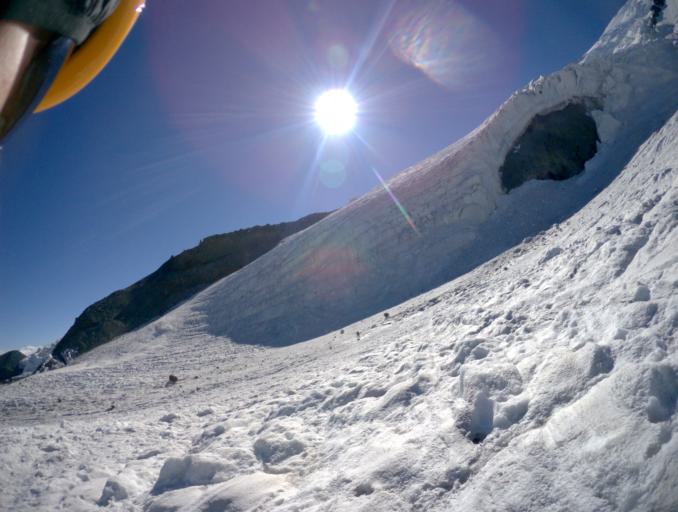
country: RU
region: Kabardino-Balkariya
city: Terskol
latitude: 43.3866
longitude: 42.4327
